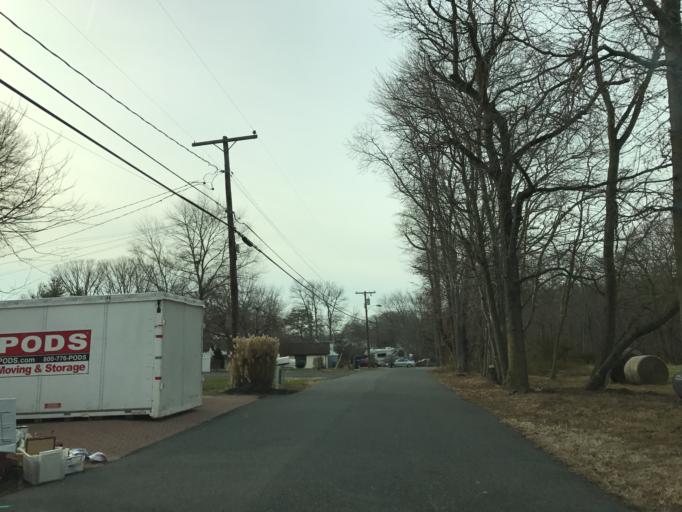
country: US
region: Maryland
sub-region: Baltimore County
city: White Marsh
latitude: 39.3849
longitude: -76.4024
